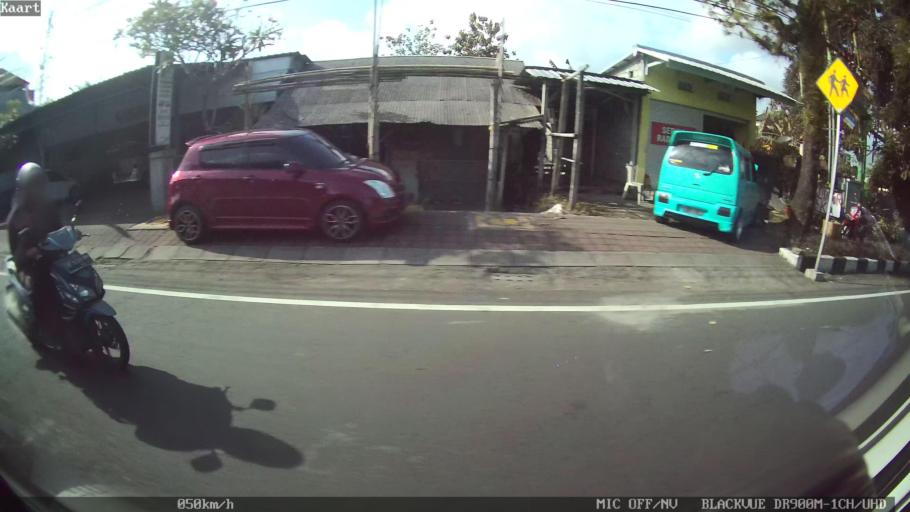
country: ID
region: Bali
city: Banjar Jumbayah
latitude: -8.5634
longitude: 115.1676
